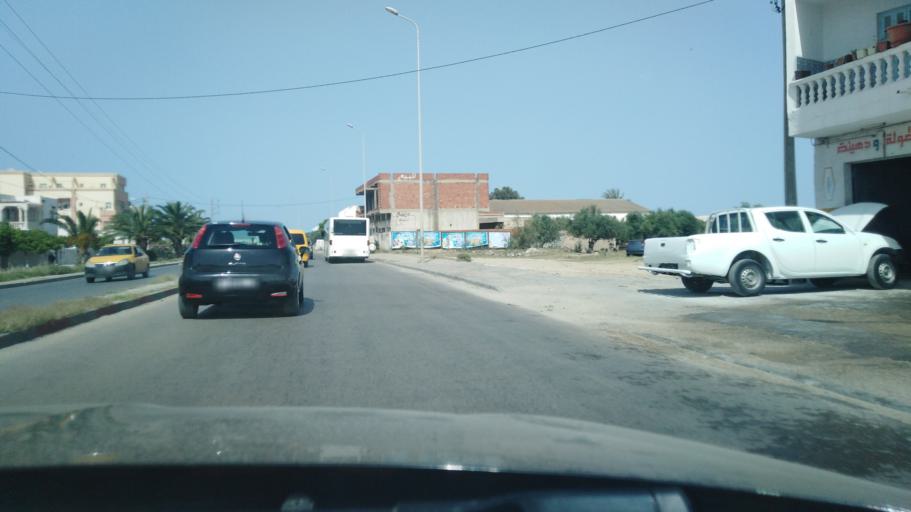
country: TN
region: Susah
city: Sousse
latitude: 35.7992
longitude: 10.6091
